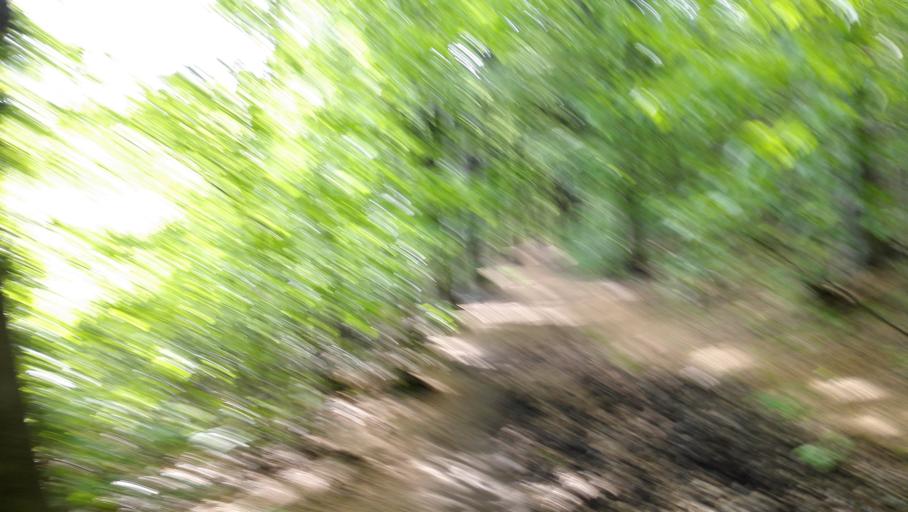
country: BE
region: Flanders
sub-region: Provincie Vlaams-Brabant
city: Holsbeek
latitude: 50.9075
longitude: 4.7700
